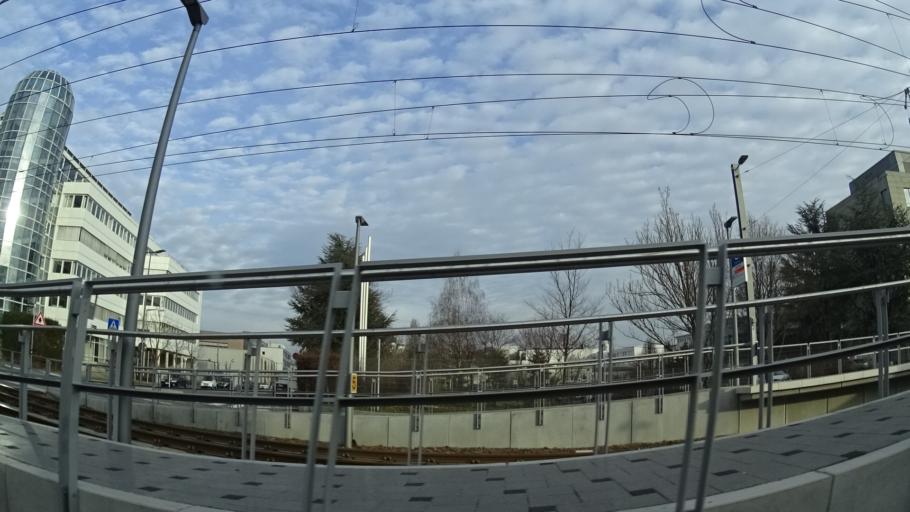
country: DE
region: Baden-Wuerttemberg
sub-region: Regierungsbezirk Stuttgart
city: Leinfelden-Echterdingen
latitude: 48.7231
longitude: 9.1211
